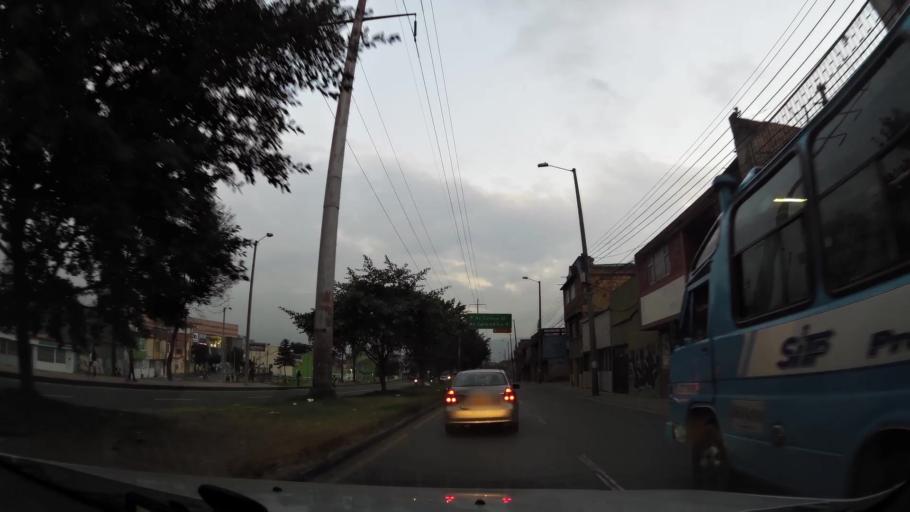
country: CO
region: Bogota D.C.
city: Bogota
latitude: 4.5882
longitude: -74.1251
